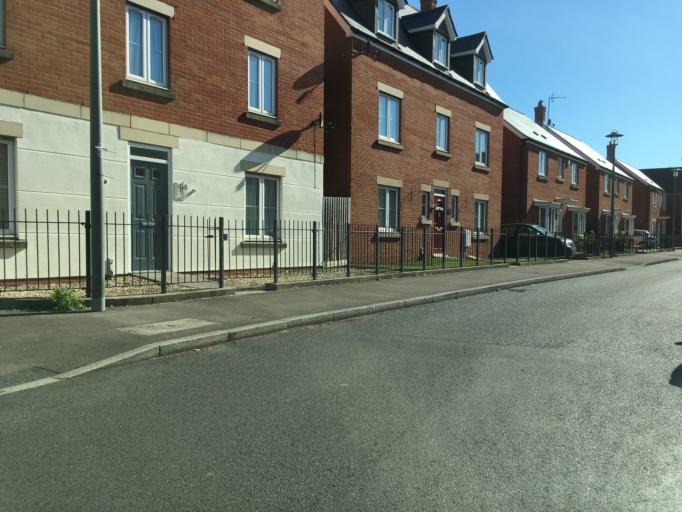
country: GB
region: England
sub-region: North Somerset
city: Portishead
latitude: 51.4882
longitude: -2.7526
